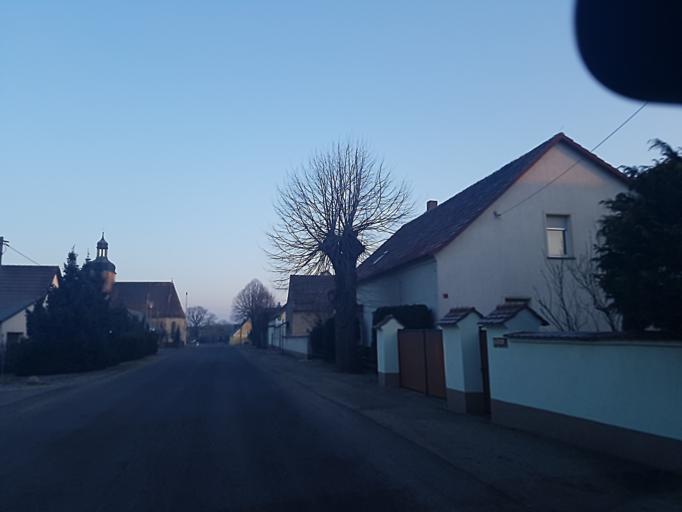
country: DE
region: Brandenburg
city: Herzberg
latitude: 51.7529
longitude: 13.2065
